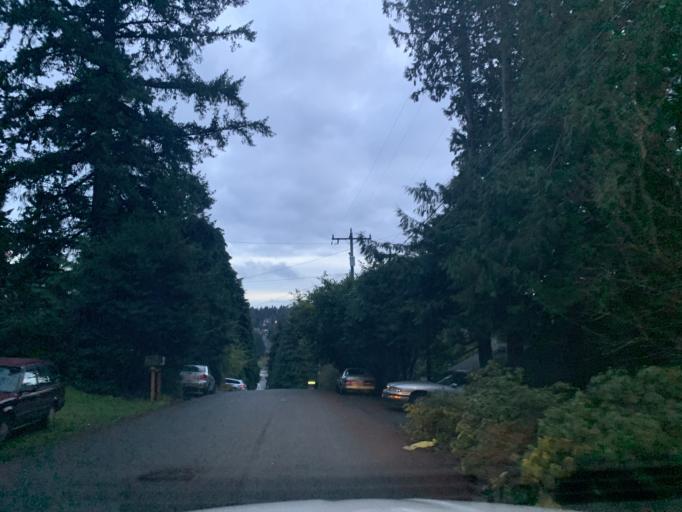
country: US
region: Washington
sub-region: King County
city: Lake Forest Park
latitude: 47.7091
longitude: -122.2854
